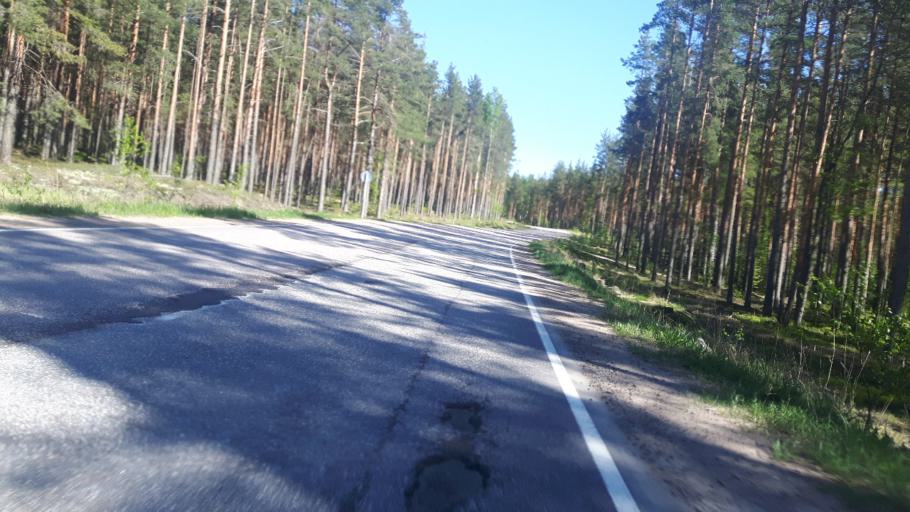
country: RU
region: Leningrad
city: Glebychevo
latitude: 60.2735
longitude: 28.9399
